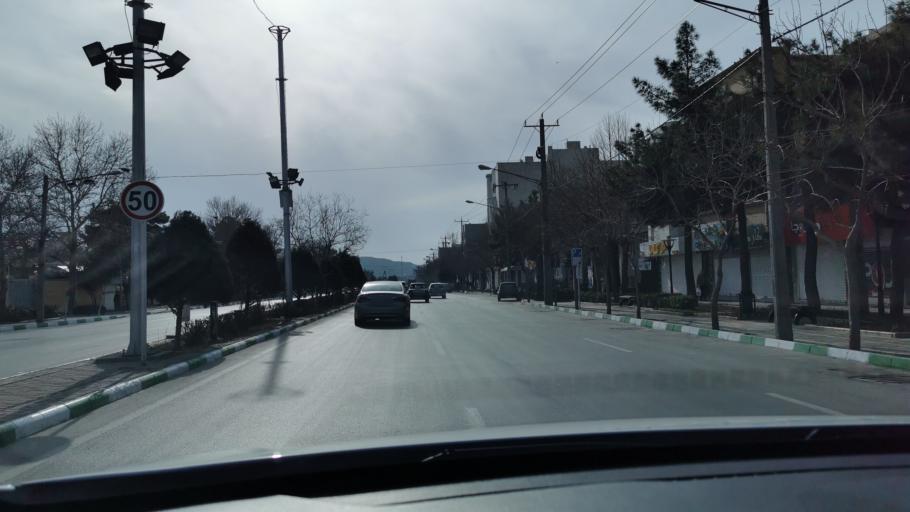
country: IR
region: Razavi Khorasan
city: Mashhad
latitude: 36.2872
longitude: 59.5440
